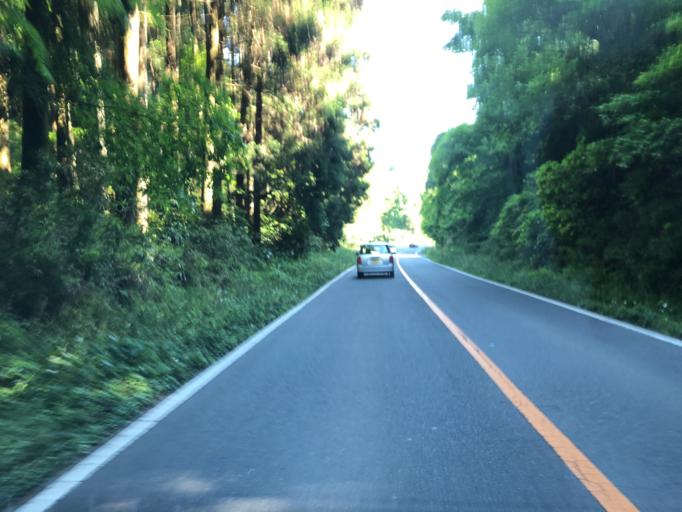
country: JP
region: Fukushima
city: Iwaki
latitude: 36.9473
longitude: 140.8244
